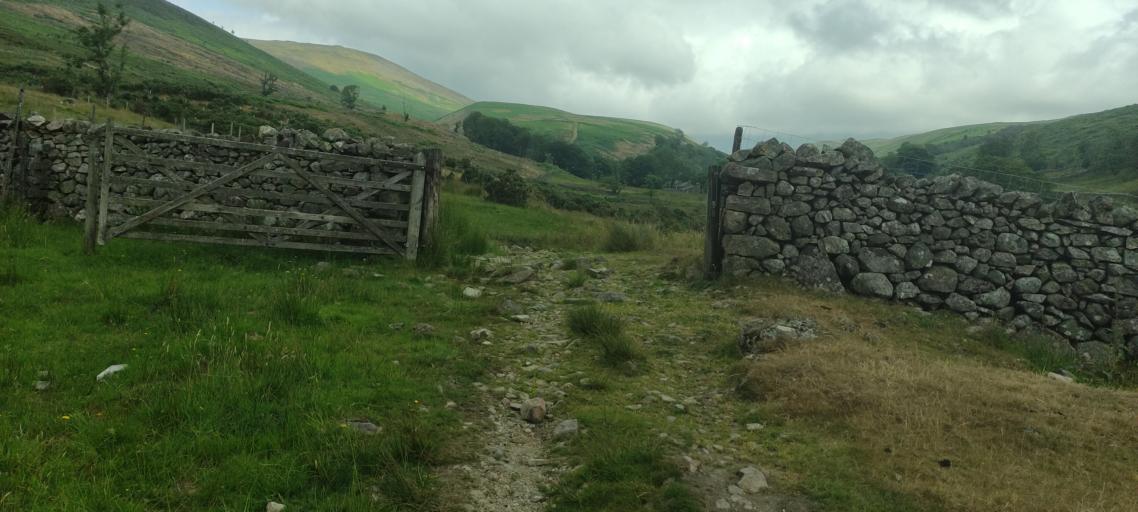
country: GB
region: England
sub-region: Cumbria
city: Seascale
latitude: 54.4069
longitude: -3.3016
